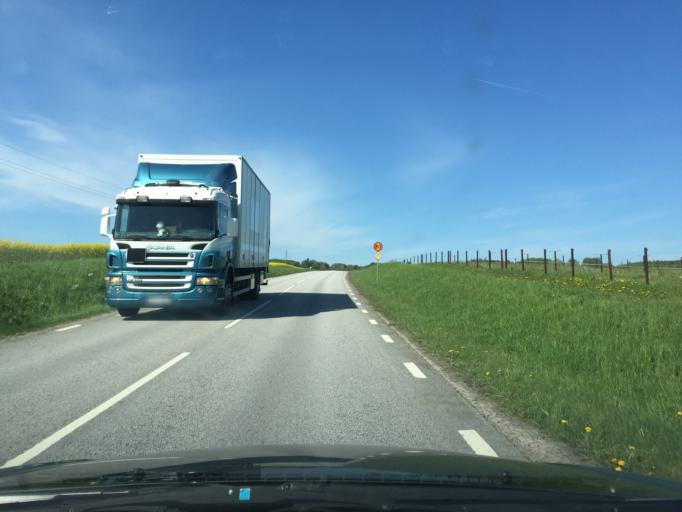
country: SE
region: Skane
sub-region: Skurups Kommun
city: Skurup
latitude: 55.5430
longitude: 13.5148
